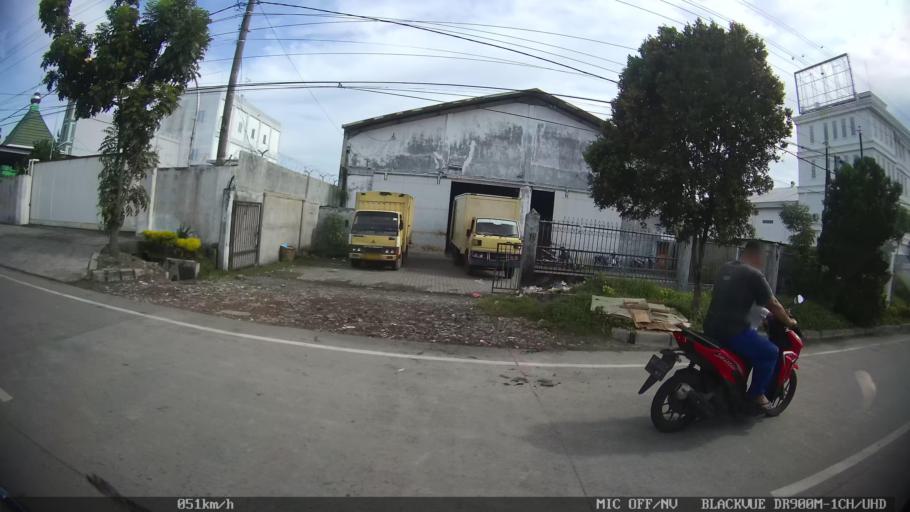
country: ID
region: North Sumatra
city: Medan
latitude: 3.6293
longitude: 98.6899
